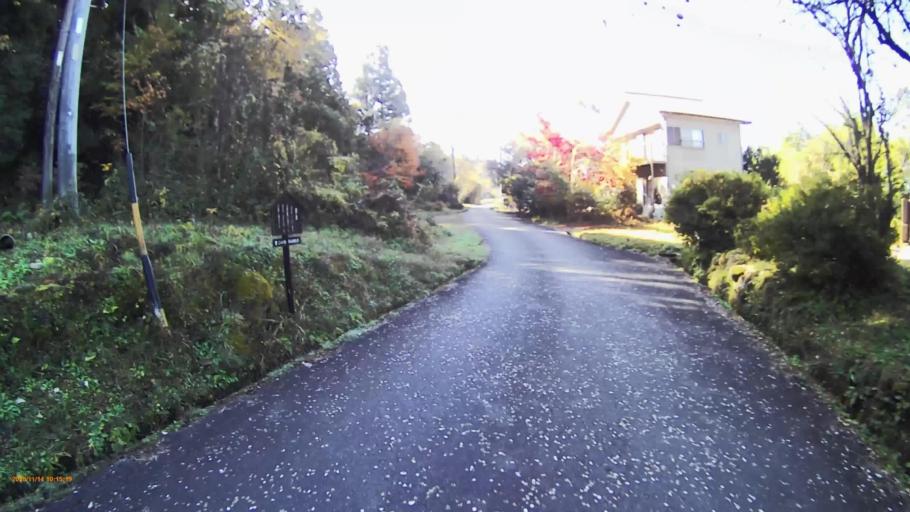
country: JP
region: Gifu
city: Nakatsugawa
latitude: 35.5117
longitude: 137.5412
